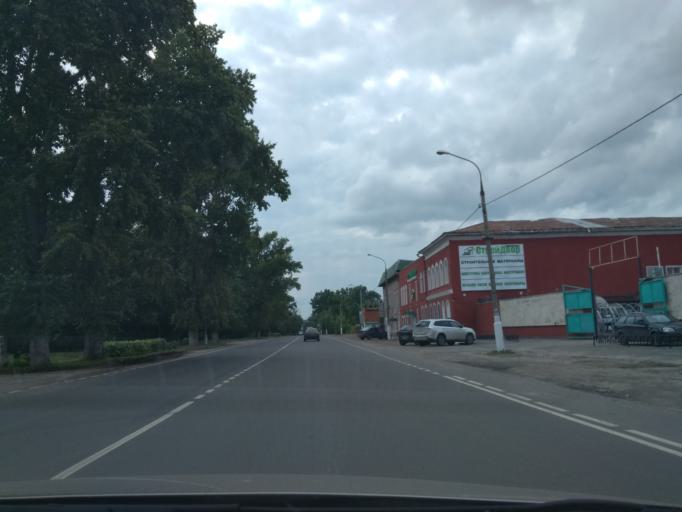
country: RU
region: Moskovskaya
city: Orekhovo-Zuyevo
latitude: 55.7975
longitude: 38.9433
